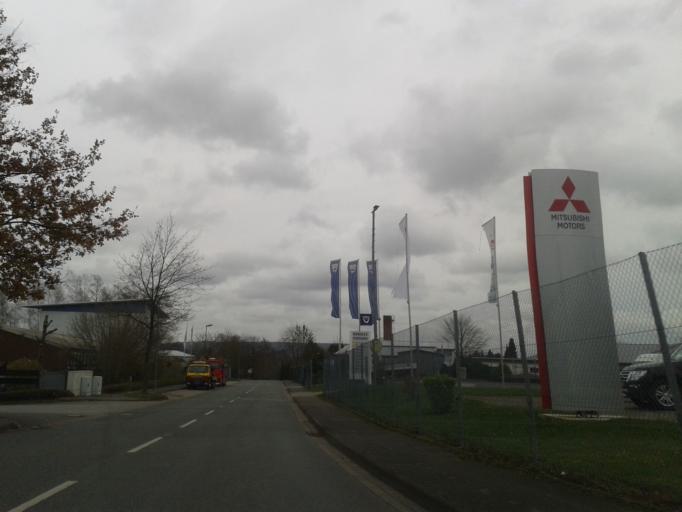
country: DE
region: North Rhine-Westphalia
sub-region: Regierungsbezirk Detmold
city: Blomberg
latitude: 51.9330
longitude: 9.0921
